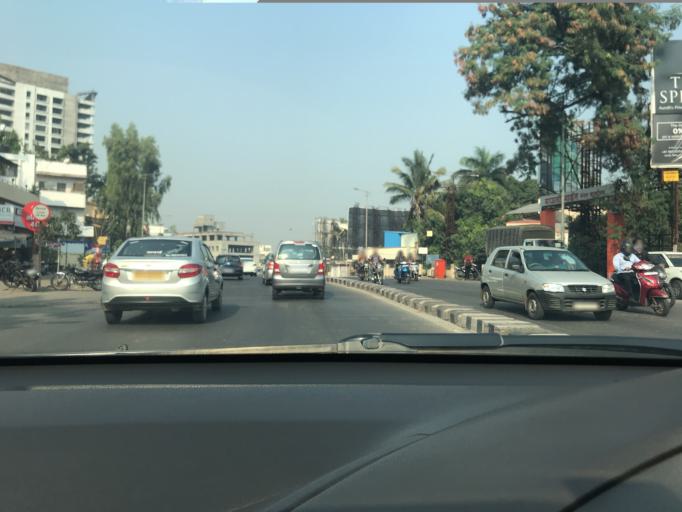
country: IN
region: Maharashtra
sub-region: Pune Division
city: Khadki
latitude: 18.5545
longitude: 73.8012
